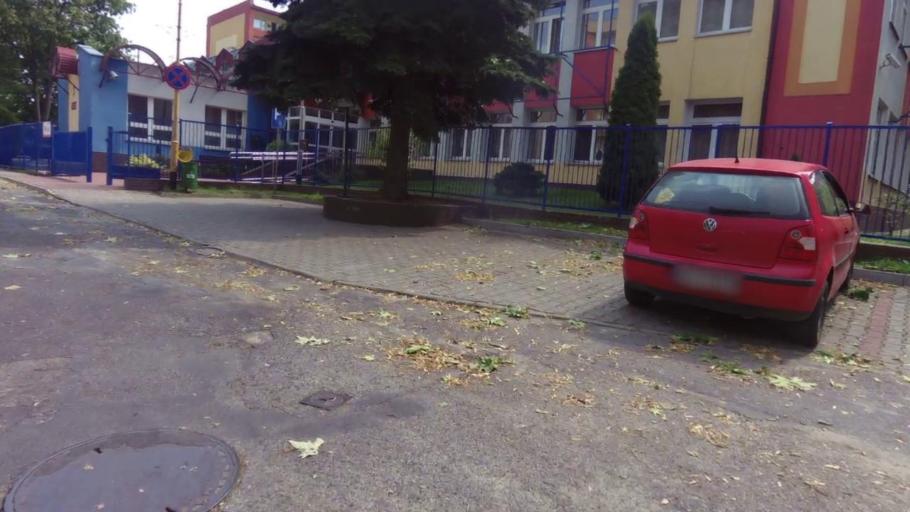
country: PL
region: West Pomeranian Voivodeship
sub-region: Powiat choszczenski
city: Choszczno
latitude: 53.1689
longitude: 15.4169
